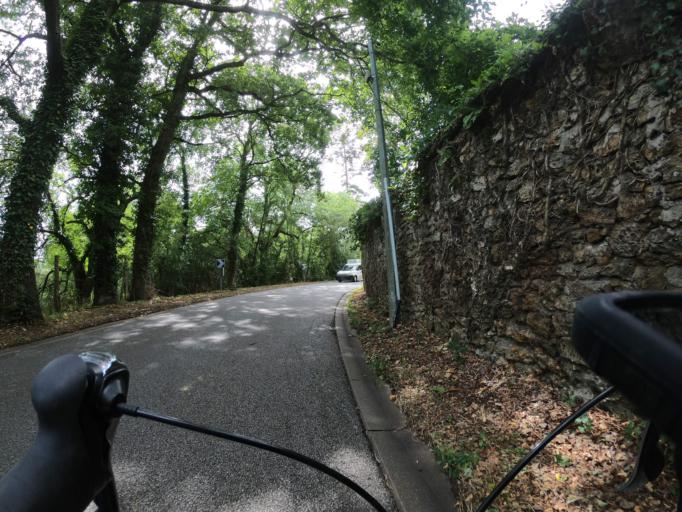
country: FR
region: Ile-de-France
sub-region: Departement des Yvelines
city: Magny-les-Hameaux
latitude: 48.7466
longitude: 2.0563
